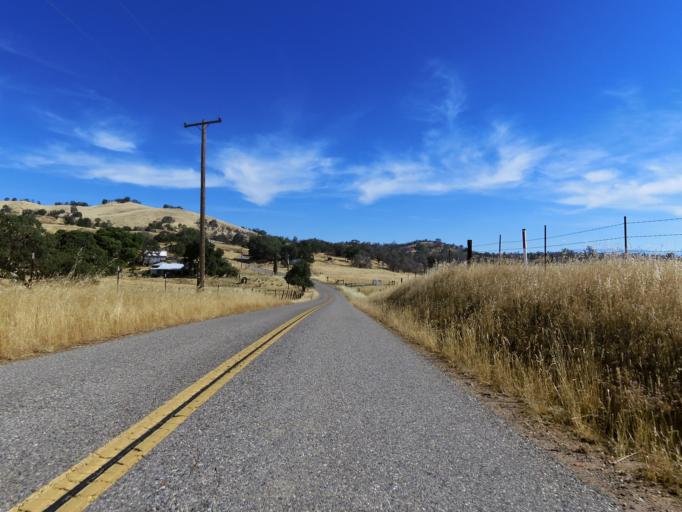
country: US
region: California
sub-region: Madera County
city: Yosemite Lakes
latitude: 37.2642
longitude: -119.9746
